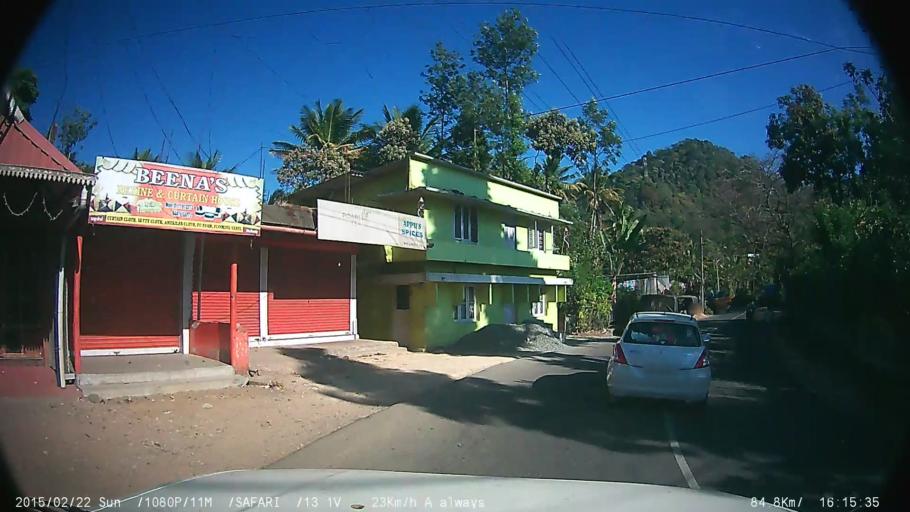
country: IN
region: Tamil Nadu
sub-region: Theni
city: Gudalur
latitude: 9.5843
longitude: 77.1067
